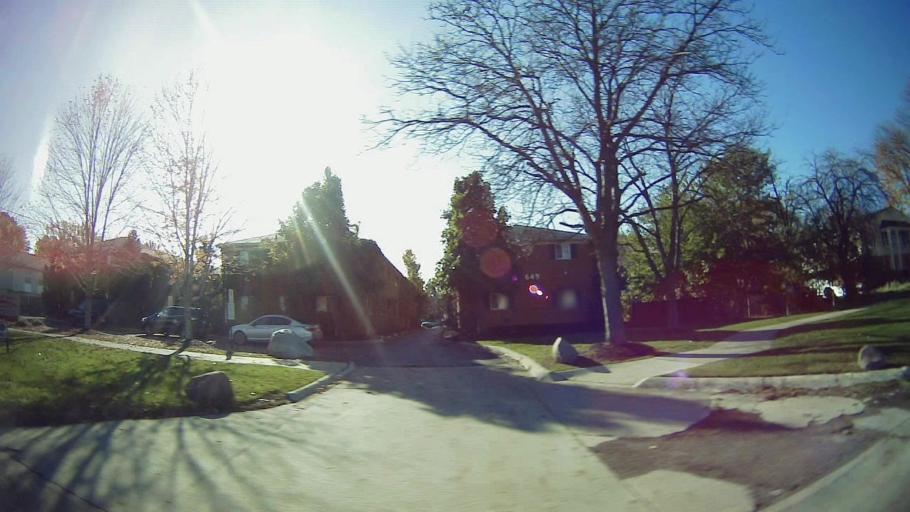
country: US
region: Michigan
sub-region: Oakland County
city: Clawson
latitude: 42.5481
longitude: -83.1558
